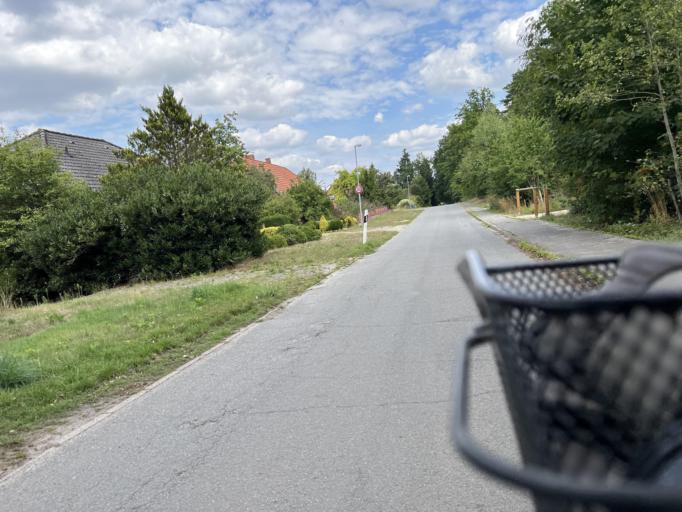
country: DE
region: Lower Saxony
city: Tosterglope
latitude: 53.1970
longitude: 10.8507
